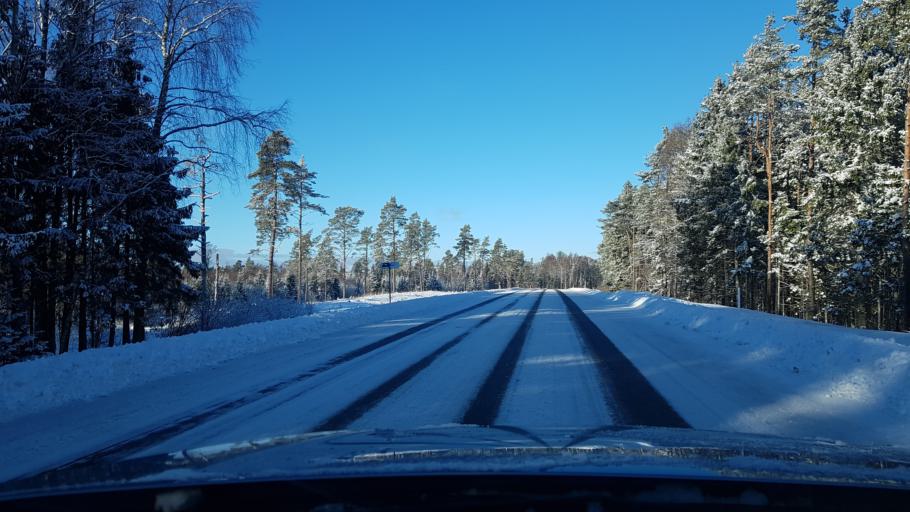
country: EE
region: Hiiumaa
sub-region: Kaerdla linn
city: Kardla
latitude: 58.9686
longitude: 22.7708
